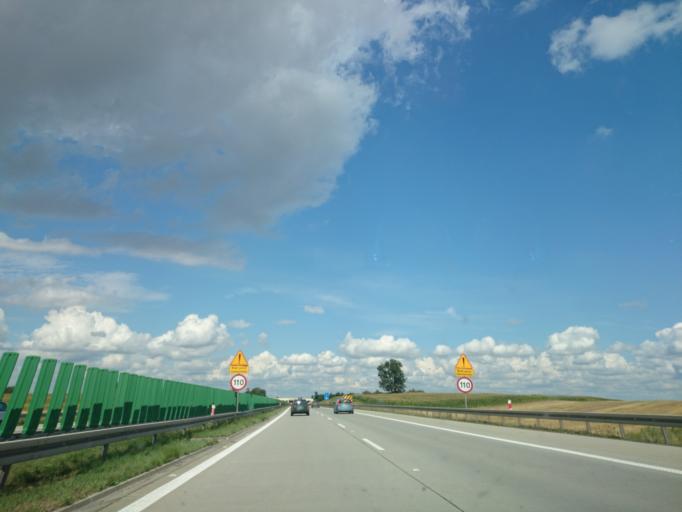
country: PL
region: Lower Silesian Voivodeship
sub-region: Powiat sredzki
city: Udanin
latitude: 51.1031
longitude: 16.4028
